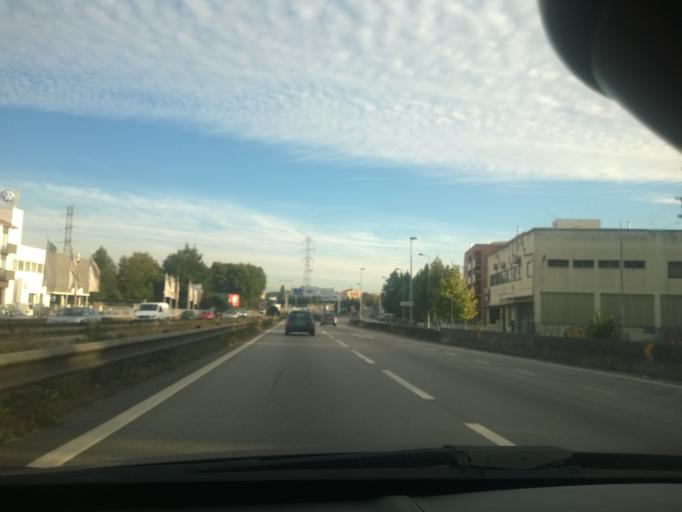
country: PT
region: Porto
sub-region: Matosinhos
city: Sao Mamede de Infesta
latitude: 41.1848
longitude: -8.6238
